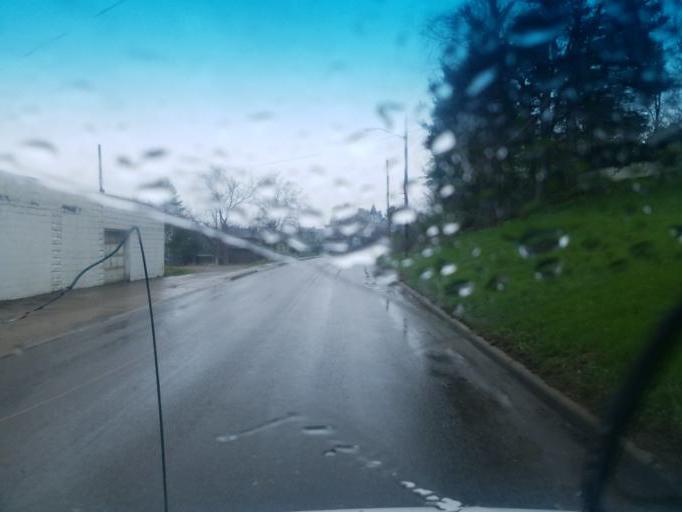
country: US
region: Ohio
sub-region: Holmes County
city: Millersburg
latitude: 40.5580
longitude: -81.9176
